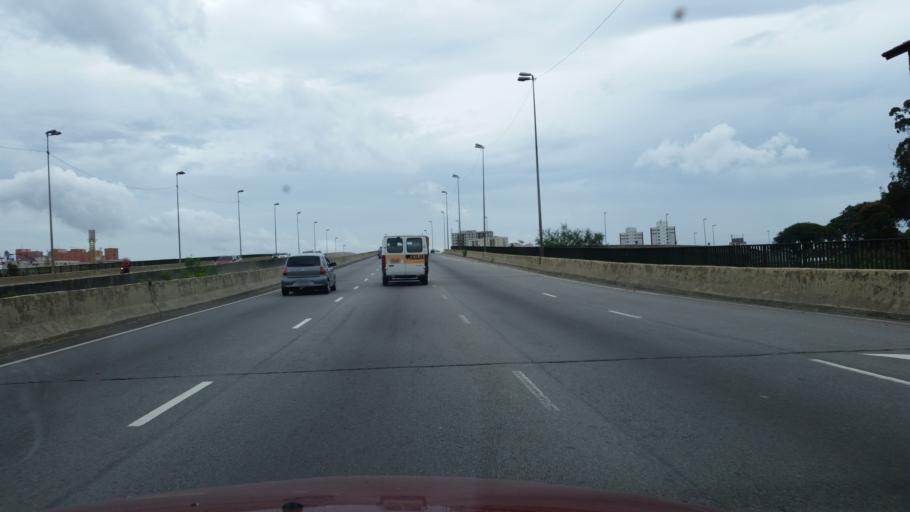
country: BR
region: Sao Paulo
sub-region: Ferraz De Vasconcelos
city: Ferraz de Vasconcelos
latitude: -23.5365
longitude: -46.4516
